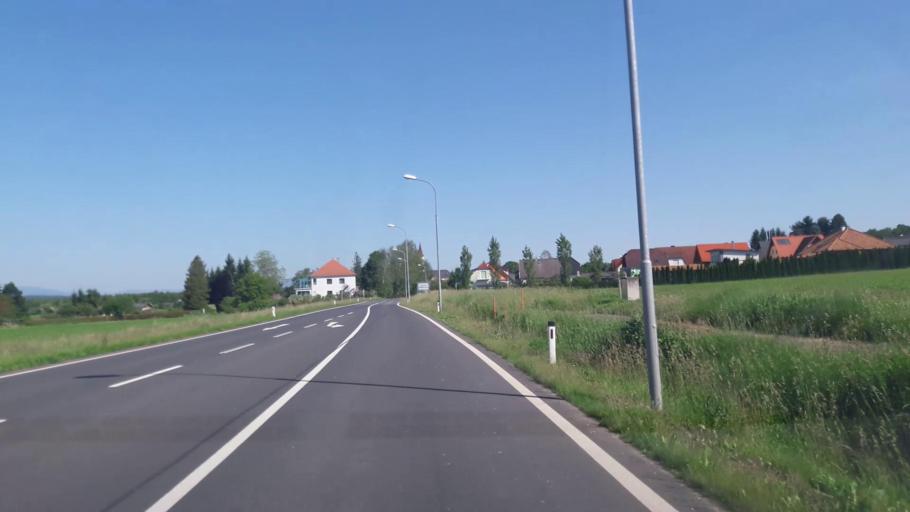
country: AT
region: Burgenland
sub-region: Politischer Bezirk Jennersdorf
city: Deutsch Kaltenbrunn
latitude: 47.0798
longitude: 16.1103
